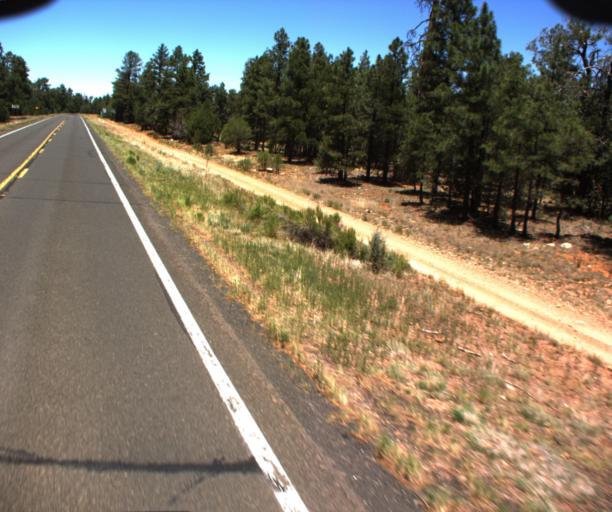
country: US
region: Arizona
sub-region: Gila County
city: Star Valley
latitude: 34.6536
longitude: -111.1086
